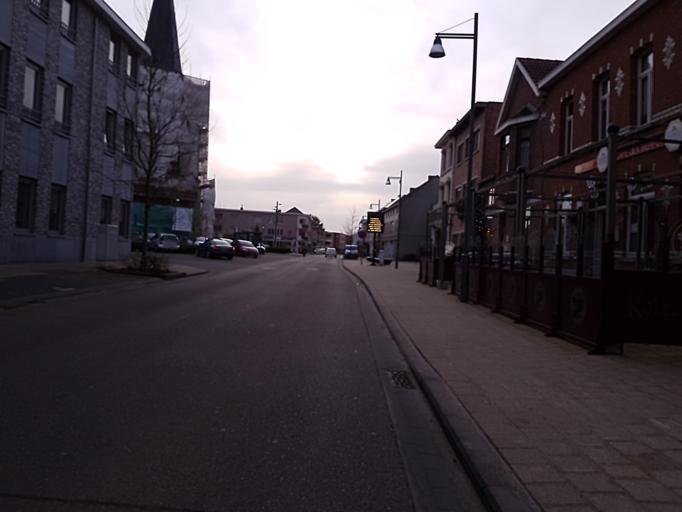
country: BE
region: Flanders
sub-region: Provincie Vlaams-Brabant
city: Tremelo
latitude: 51.0289
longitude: 4.6941
